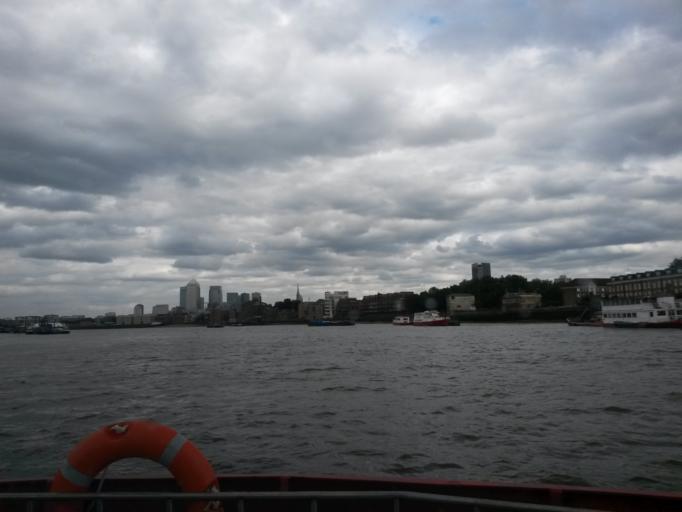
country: GB
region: England
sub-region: Greater London
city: Bethnal Green
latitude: 51.5017
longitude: -0.0625
